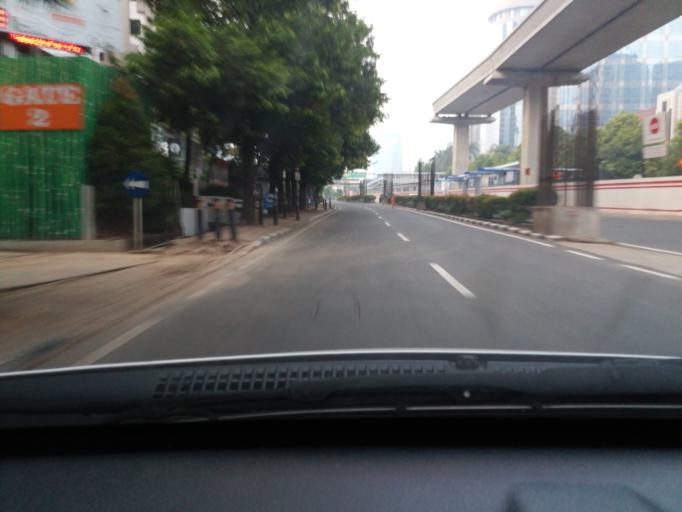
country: ID
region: Jakarta Raya
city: Jakarta
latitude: -6.2191
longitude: 106.8315
